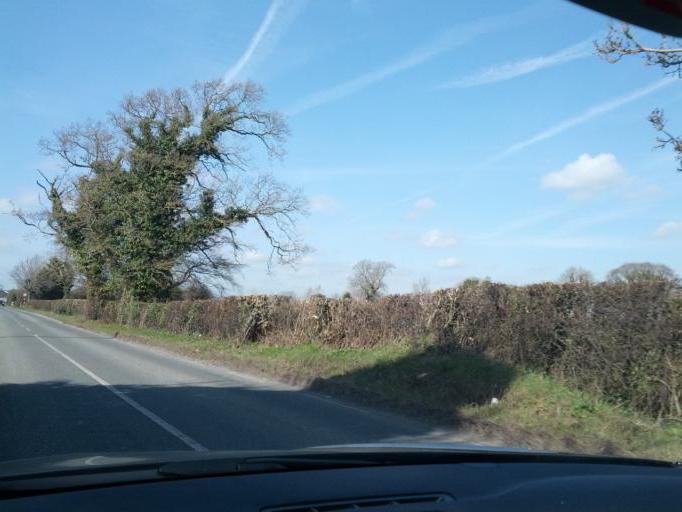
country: IE
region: Leinster
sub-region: Kildare
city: Maynooth
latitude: 53.3685
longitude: -6.5761
